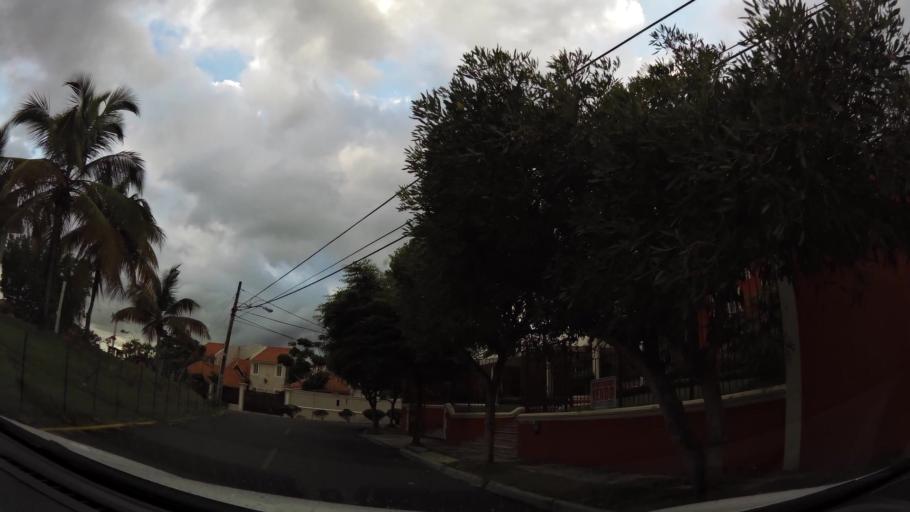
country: DO
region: Nacional
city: Santo Domingo
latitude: 18.5016
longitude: -69.9676
